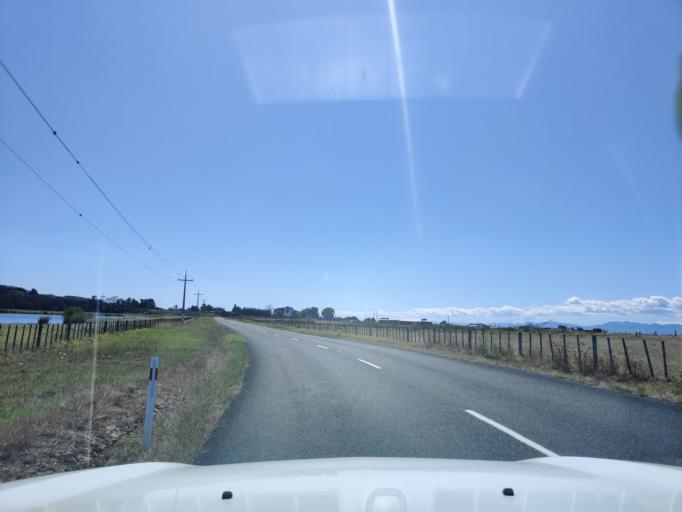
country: NZ
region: Waikato
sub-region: Thames-Coromandel District
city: Thames
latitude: -37.0643
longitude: 175.2984
